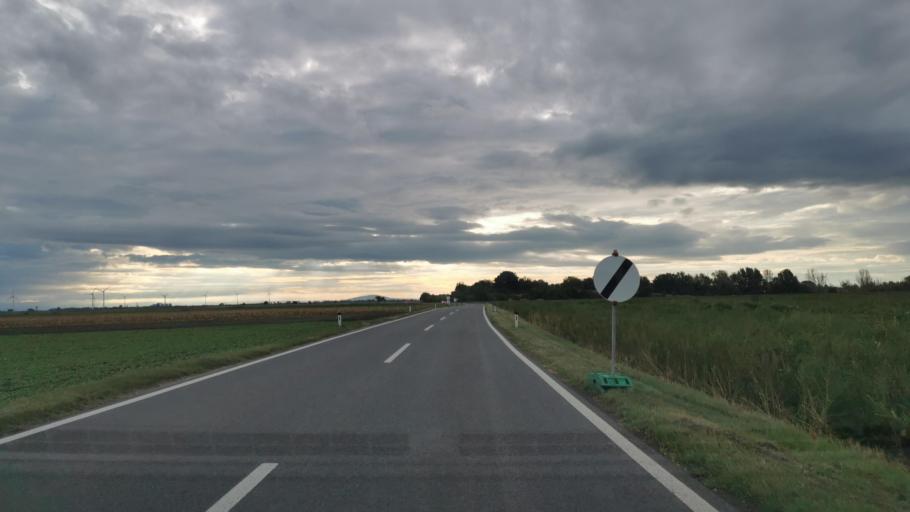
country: AT
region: Lower Austria
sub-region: Politischer Bezirk Ganserndorf
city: Grosshofen
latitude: 48.2300
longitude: 16.6141
